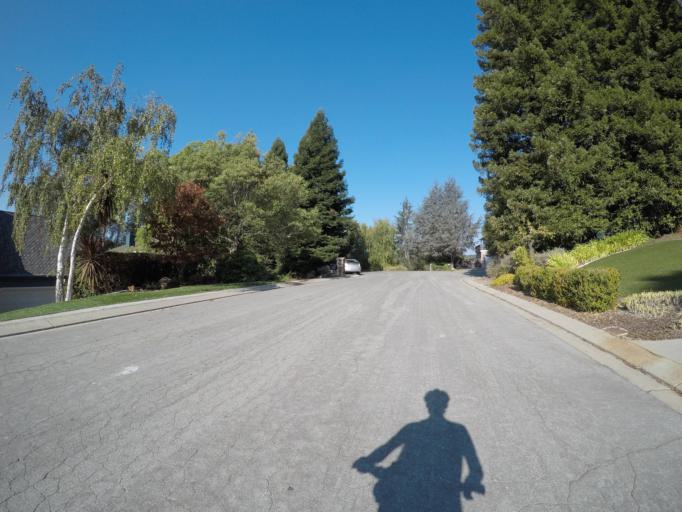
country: US
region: California
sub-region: Santa Cruz County
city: Scotts Valley
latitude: 37.0426
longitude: -122.0232
